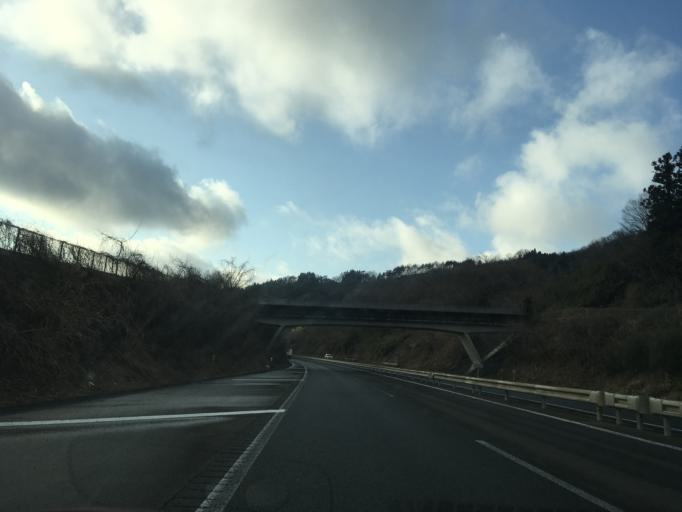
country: JP
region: Miyagi
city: Okawara
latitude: 38.1435
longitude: 140.7195
